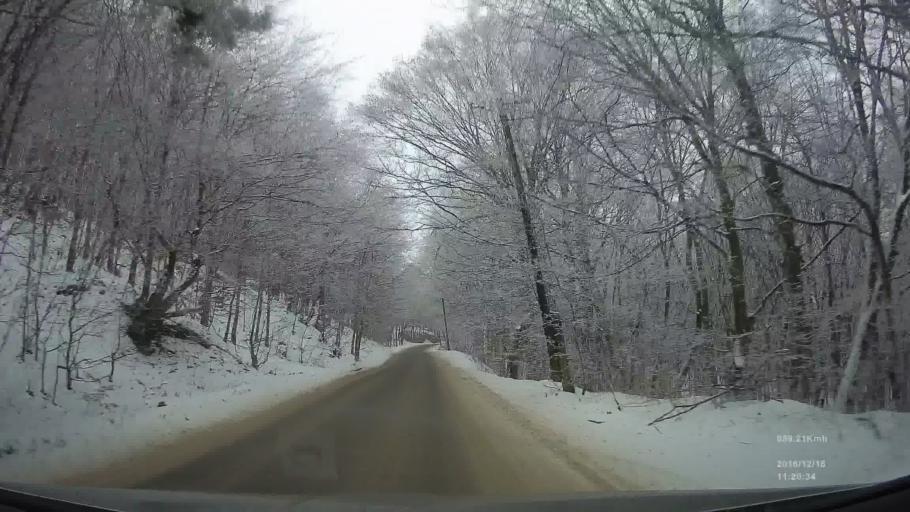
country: SK
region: Presovsky
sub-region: Okres Presov
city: Presov
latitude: 48.9095
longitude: 21.3613
